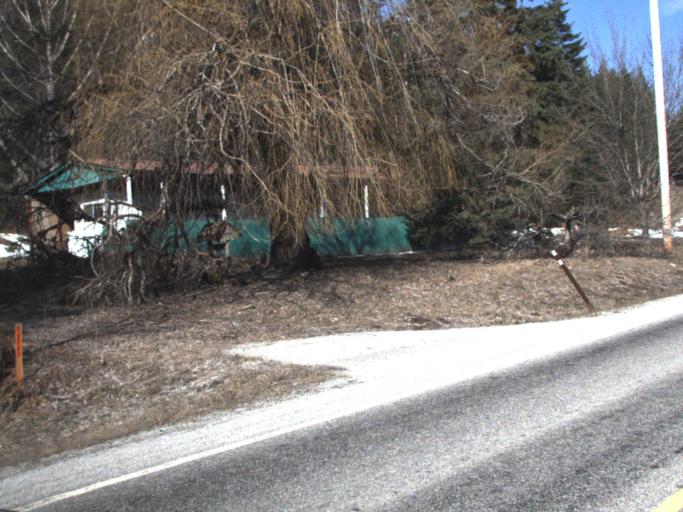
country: CA
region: British Columbia
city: Fruitvale
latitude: 48.6469
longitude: -117.3784
